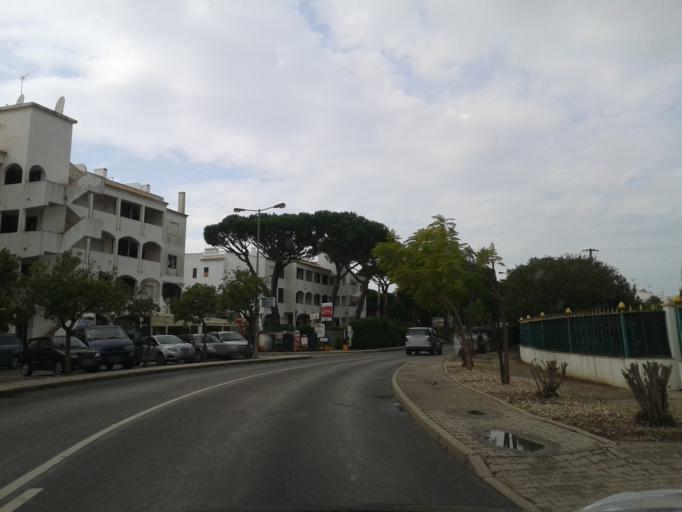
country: PT
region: Faro
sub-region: Loule
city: Boliqueime
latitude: 37.0966
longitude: -8.1757
